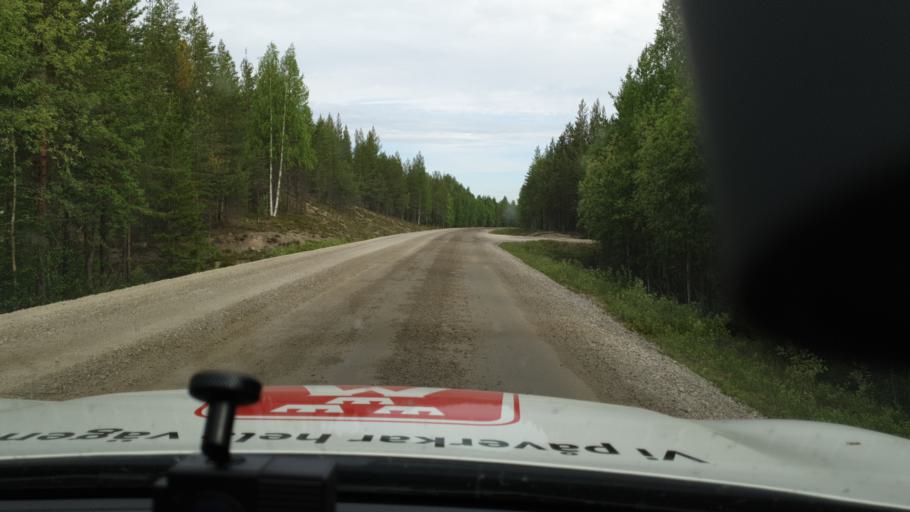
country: SE
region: Vaesterbotten
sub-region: Lycksele Kommun
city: Lycksele
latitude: 64.8423
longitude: 18.7648
